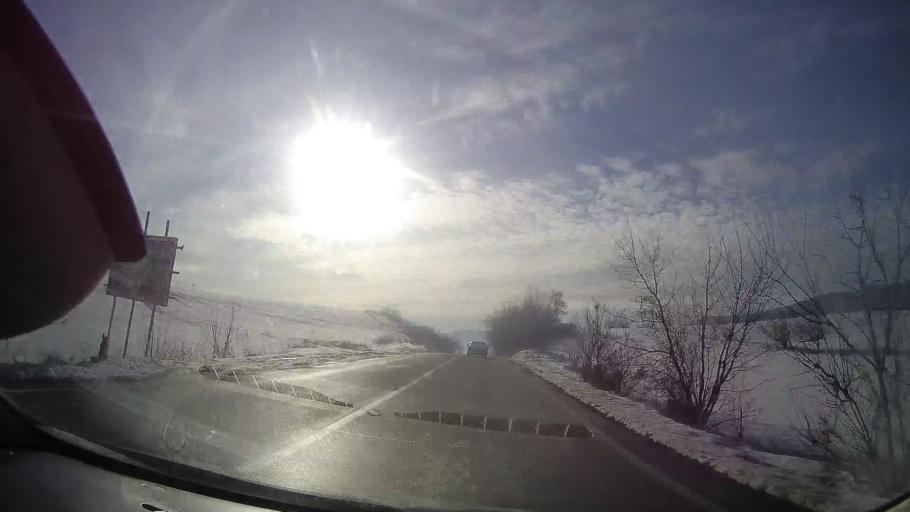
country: RO
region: Neamt
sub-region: Comuna Garcina
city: Garcina
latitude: 46.9968
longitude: 26.3671
